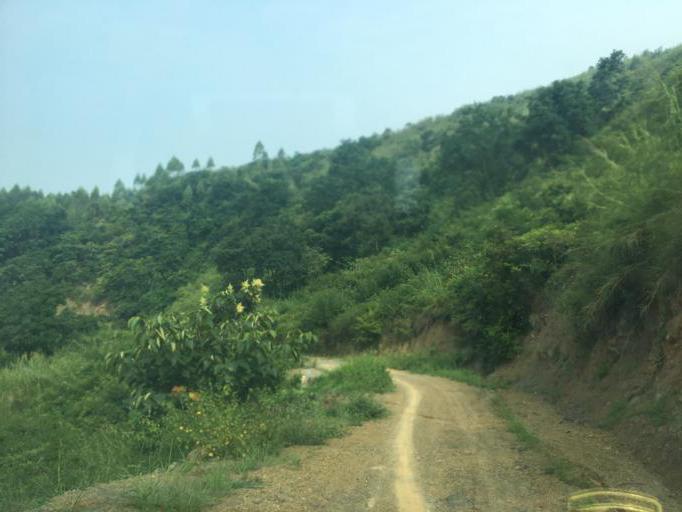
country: CN
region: Guizhou Sheng
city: Anshun
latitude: 25.4478
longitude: 105.9456
